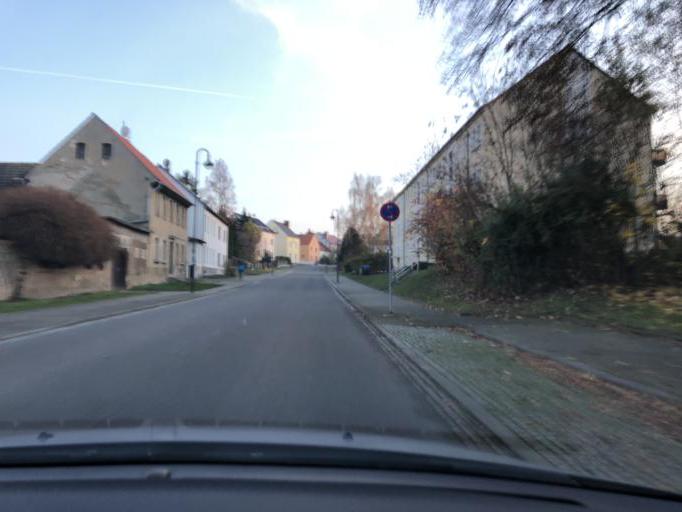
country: DE
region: Saxony
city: Nerchau
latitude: 51.2669
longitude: 12.7927
